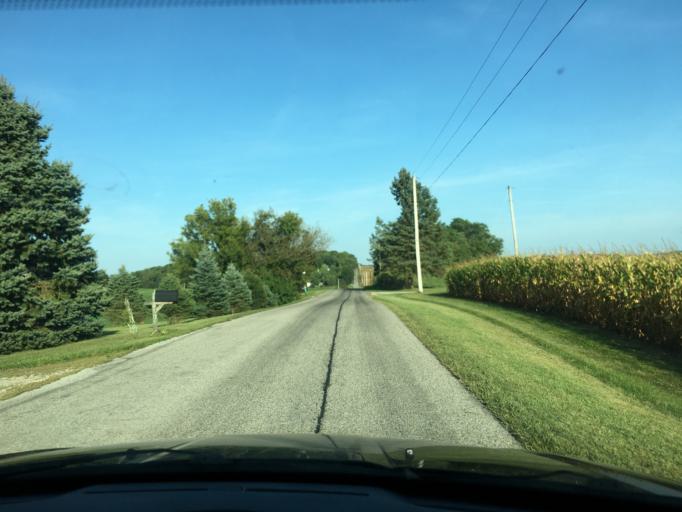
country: US
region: Ohio
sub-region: Logan County
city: West Liberty
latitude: 40.2993
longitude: -83.7439
